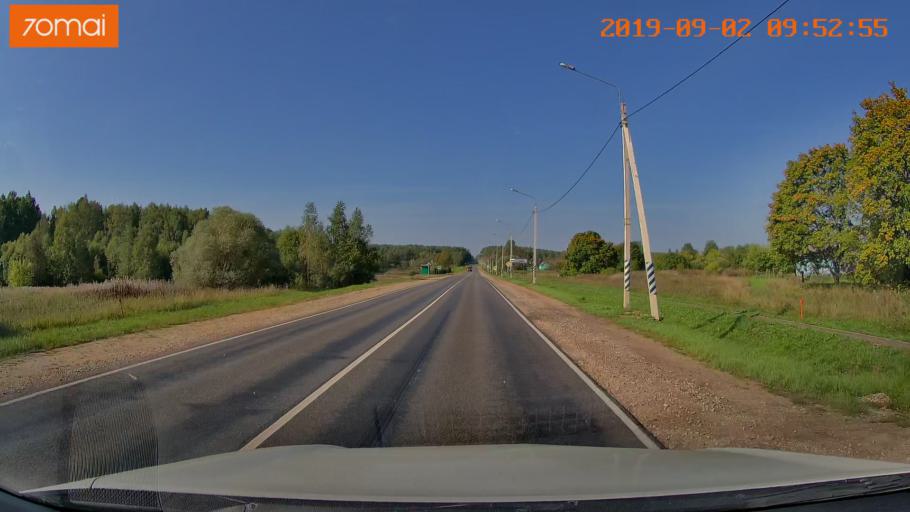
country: RU
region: Kaluga
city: Mosal'sk
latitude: 54.5863
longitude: 34.6863
